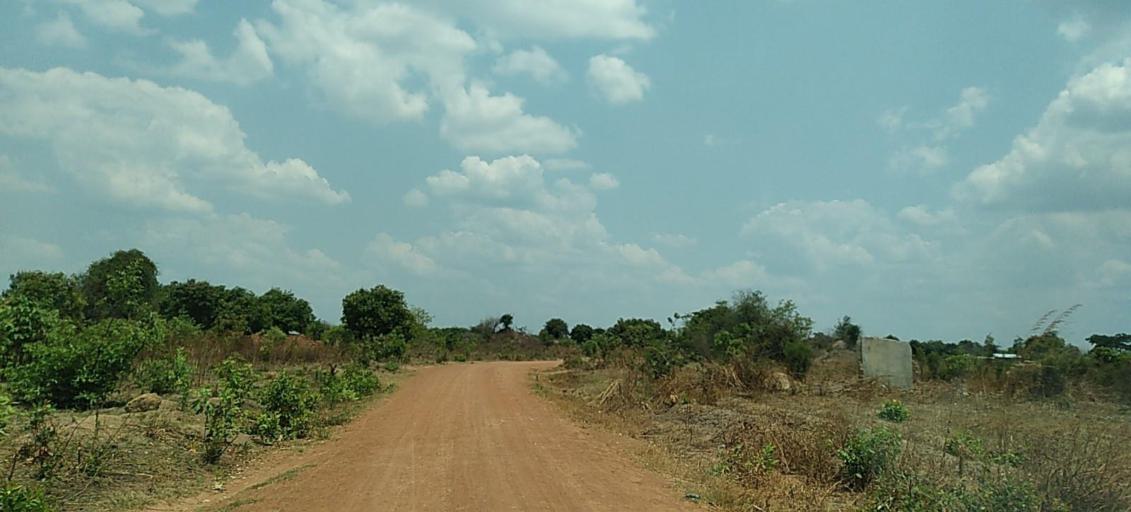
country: ZM
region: Copperbelt
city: Luanshya
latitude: -13.1305
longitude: 28.3129
